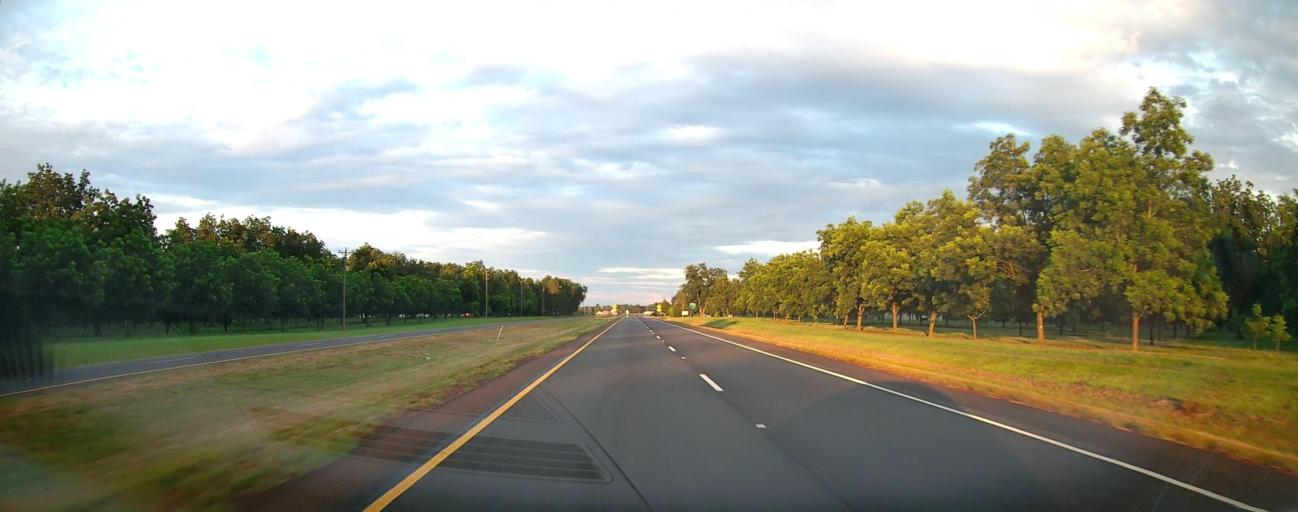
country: US
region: Georgia
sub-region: Peach County
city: Fort Valley
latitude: 32.5777
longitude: -83.8794
